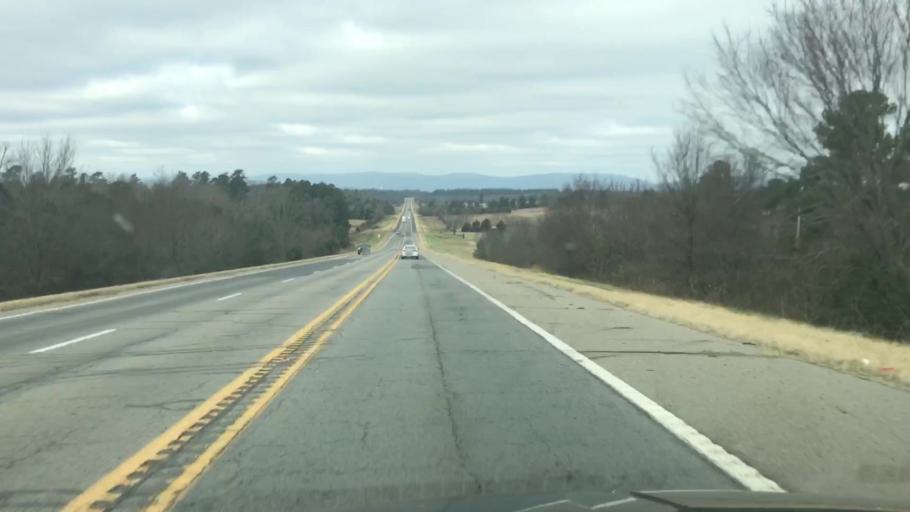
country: US
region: Arkansas
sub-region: Scott County
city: Waldron
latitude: 34.8672
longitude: -94.0772
